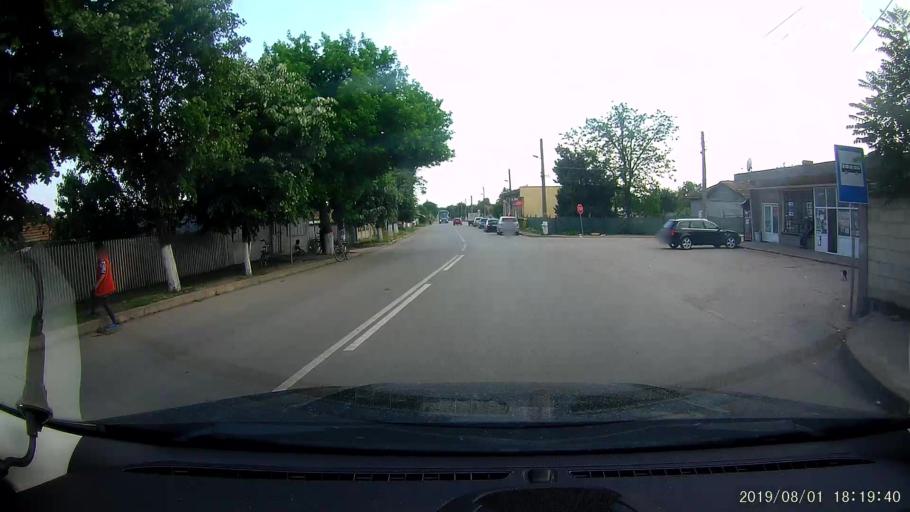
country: BG
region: Shumen
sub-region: Obshtina Kaolinovo
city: Kaolinovo
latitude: 43.6813
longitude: 27.0910
